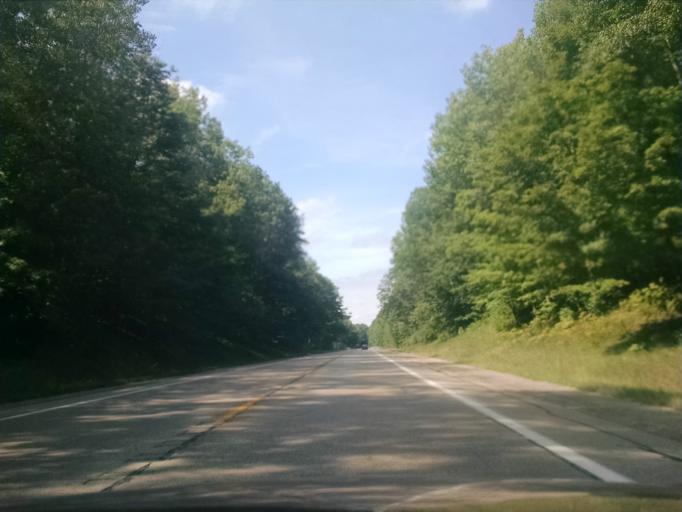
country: US
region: Michigan
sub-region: Clare County
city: Clare
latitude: 43.8751
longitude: -84.9462
